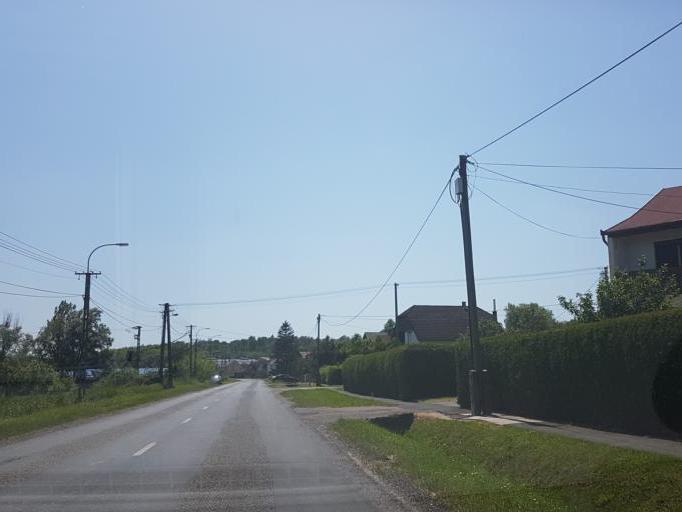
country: HU
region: Zala
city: Zalaegerszeg
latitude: 46.8483
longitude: 16.7741
